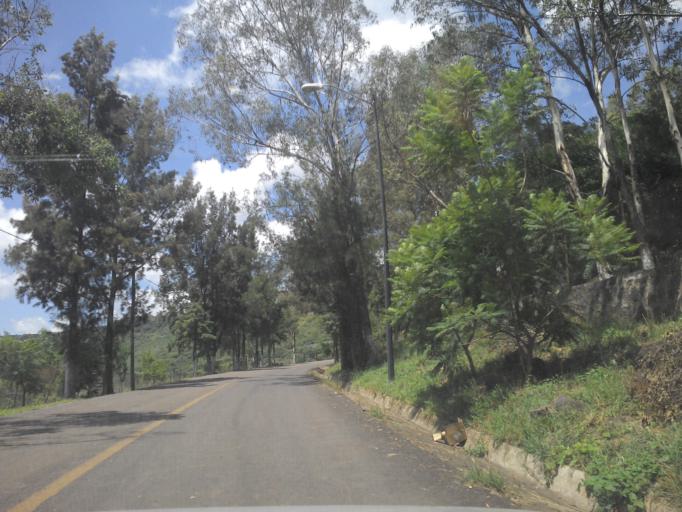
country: MX
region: Jalisco
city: Atotonilco el Alto
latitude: 20.5673
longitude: -102.5131
